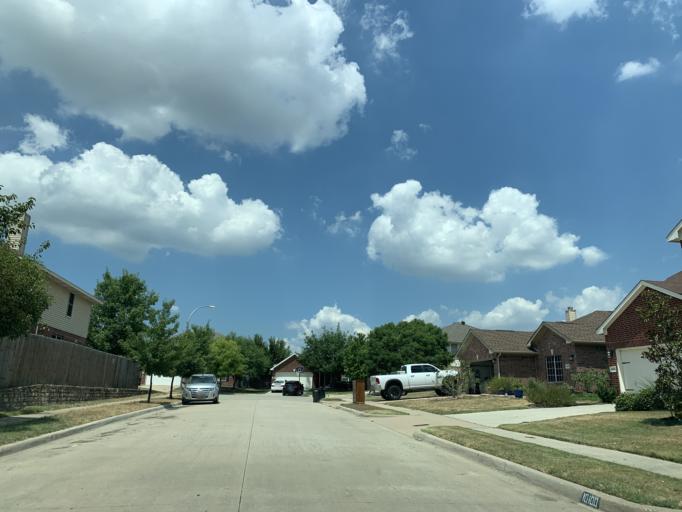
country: US
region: Texas
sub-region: Tarrant County
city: White Settlement
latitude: 32.7273
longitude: -97.5010
